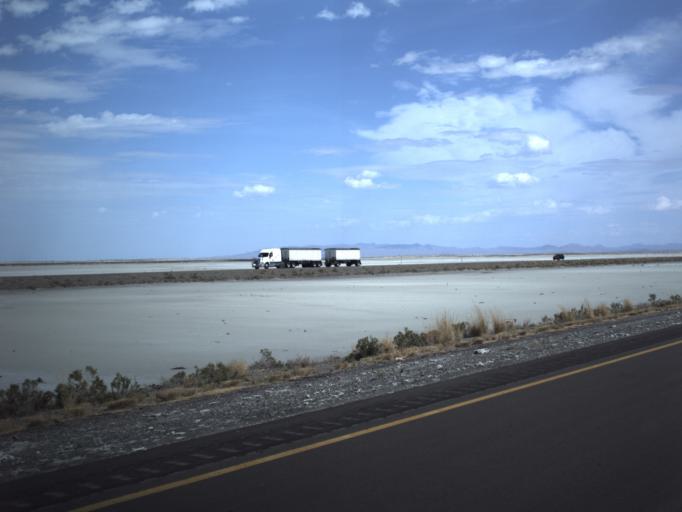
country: US
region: Utah
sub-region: Tooele County
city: Wendover
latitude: 40.7302
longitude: -113.4710
